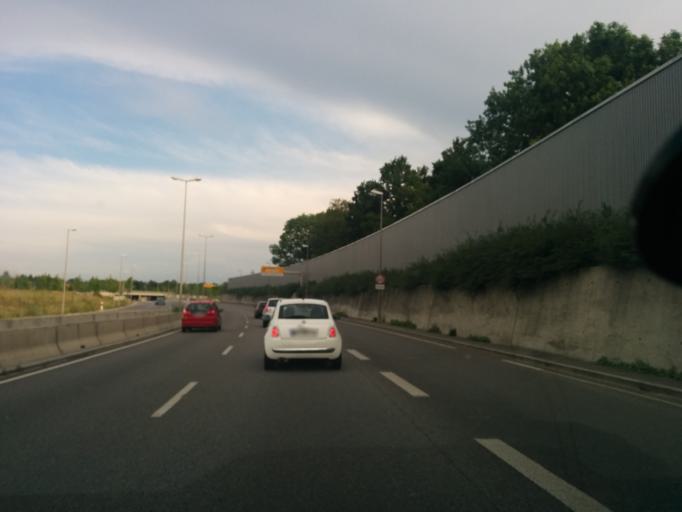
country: DE
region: Bavaria
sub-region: Swabia
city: Stadtbergen
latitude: 48.3552
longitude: 10.8522
